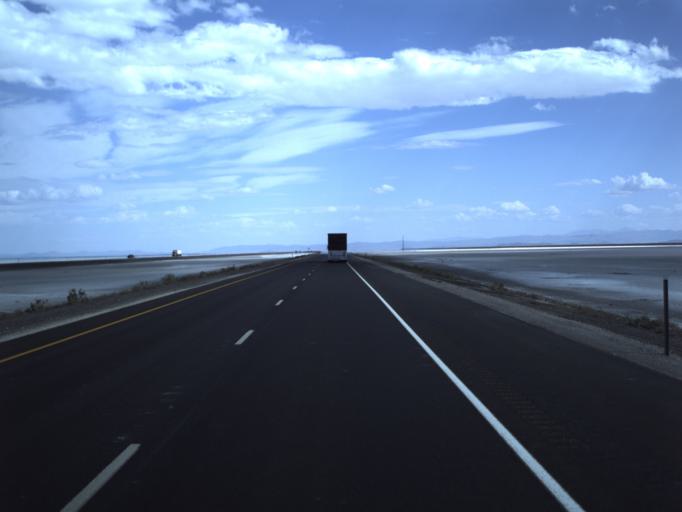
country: US
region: Utah
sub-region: Tooele County
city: Wendover
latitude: 40.7337
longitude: -113.6228
